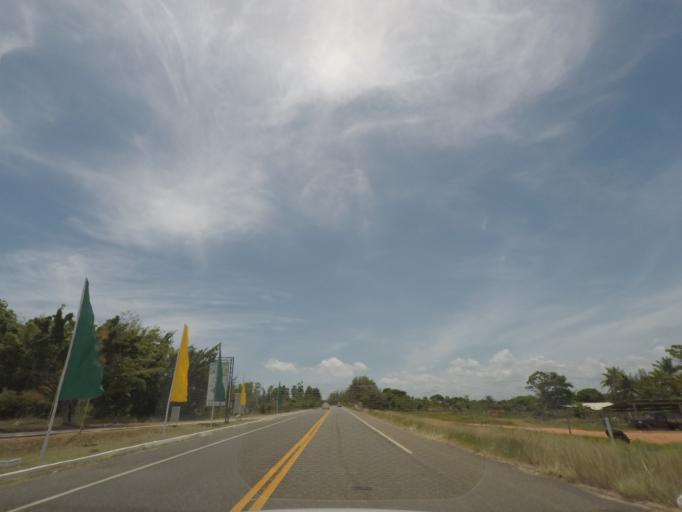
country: BR
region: Bahia
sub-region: Entre Rios
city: Entre Rios
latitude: -12.3021
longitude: -37.9004
